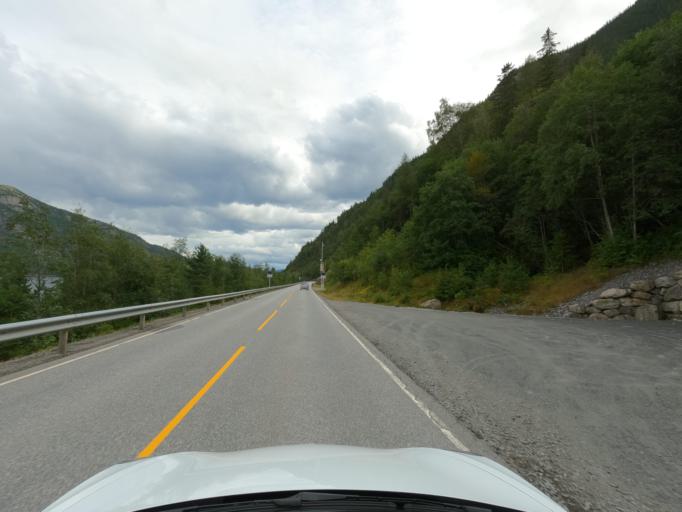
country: NO
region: Telemark
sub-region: Hjartdal
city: Sauland
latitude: 59.9022
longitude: 8.8903
